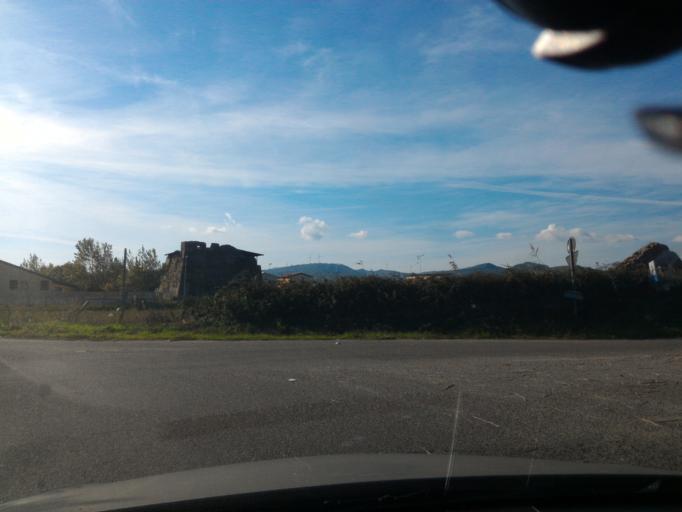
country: IT
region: Calabria
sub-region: Provincia di Crotone
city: Ciro Marina
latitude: 39.3557
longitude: 17.1298
